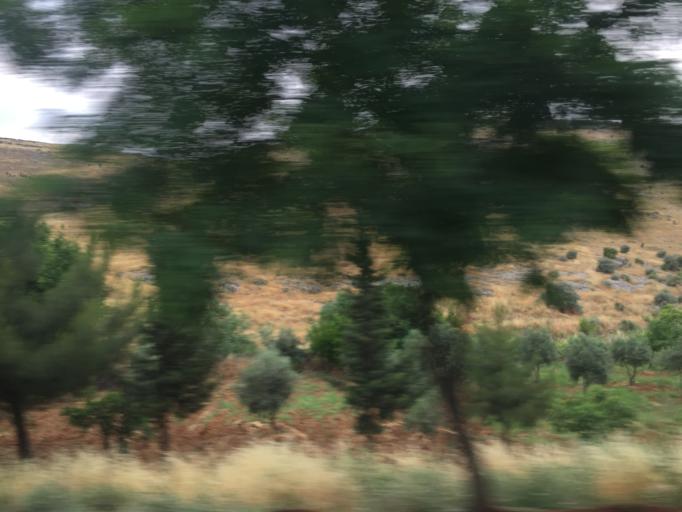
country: TR
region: Gaziantep
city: Yesildere
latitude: 36.9936
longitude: 37.4462
